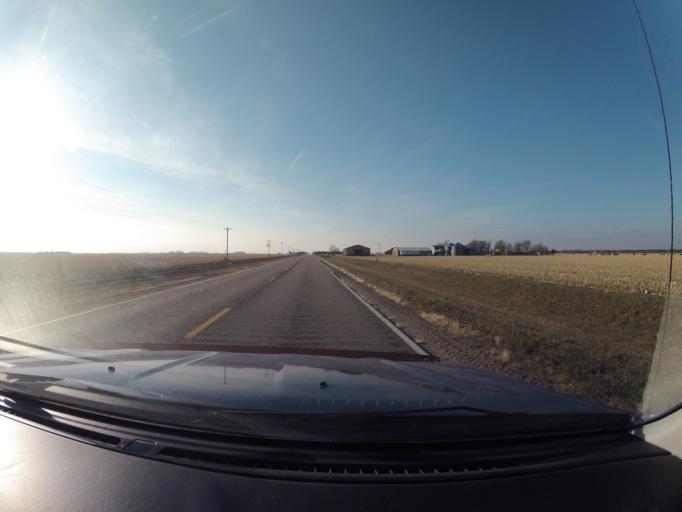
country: US
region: Nebraska
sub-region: Buffalo County
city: Kearney
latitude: 40.6410
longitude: -99.0110
